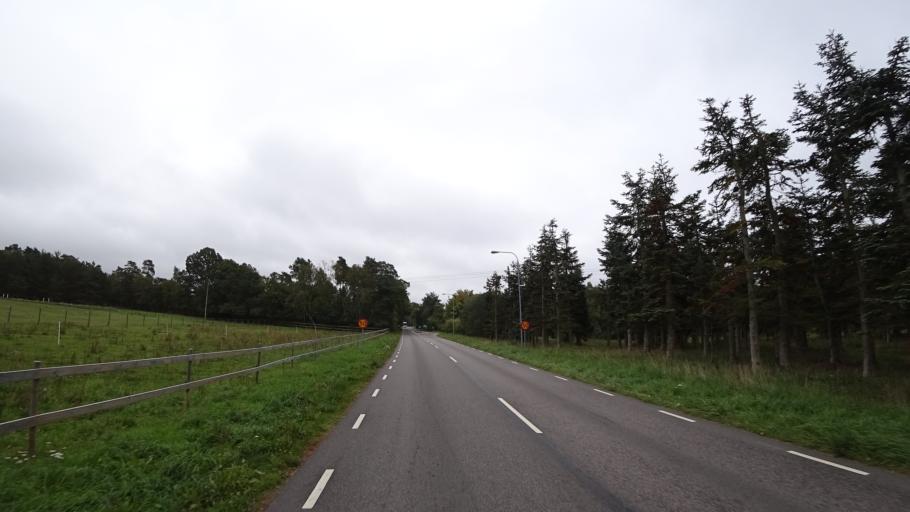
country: SE
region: Skane
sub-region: Kavlinge Kommun
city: Hofterup
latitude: 55.8199
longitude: 12.9713
